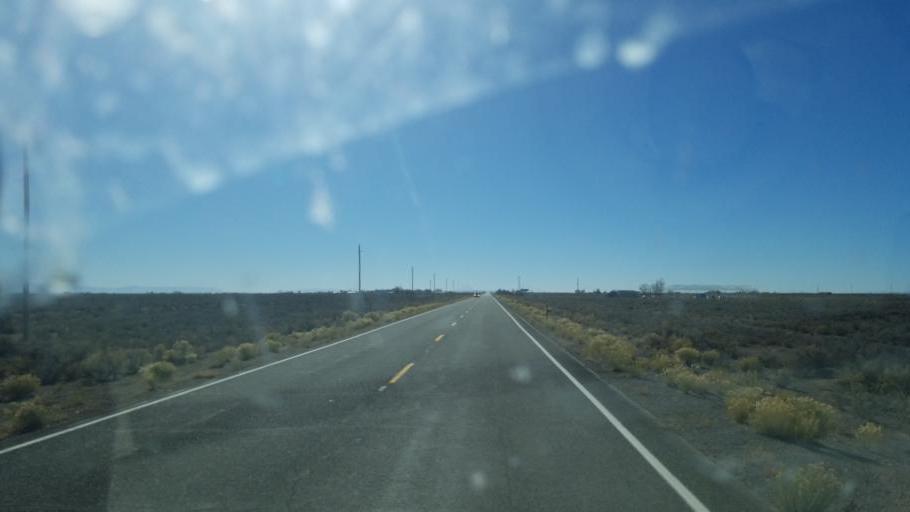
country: US
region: Colorado
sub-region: Saguache County
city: Center
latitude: 37.7685
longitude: -105.8830
